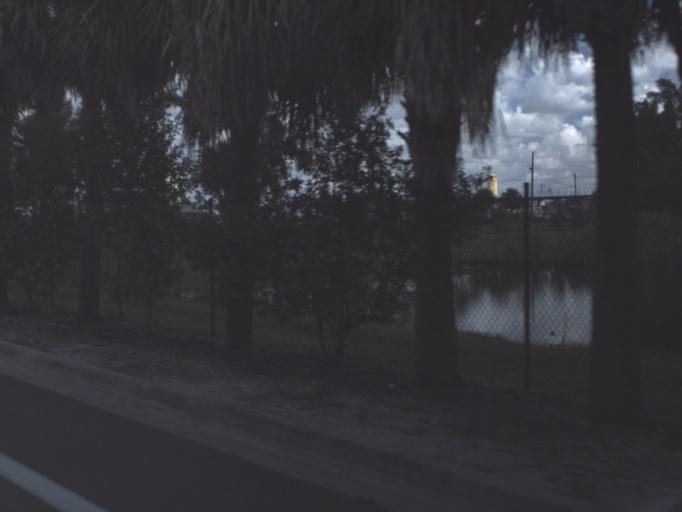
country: US
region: Florida
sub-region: Lee County
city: Fort Myers
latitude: 26.6256
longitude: -81.8600
